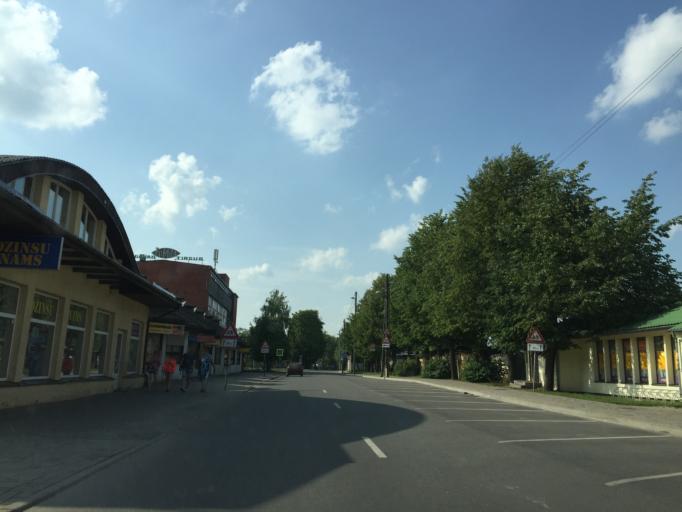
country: LV
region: Jelgava
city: Jelgava
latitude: 56.6565
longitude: 23.7216
